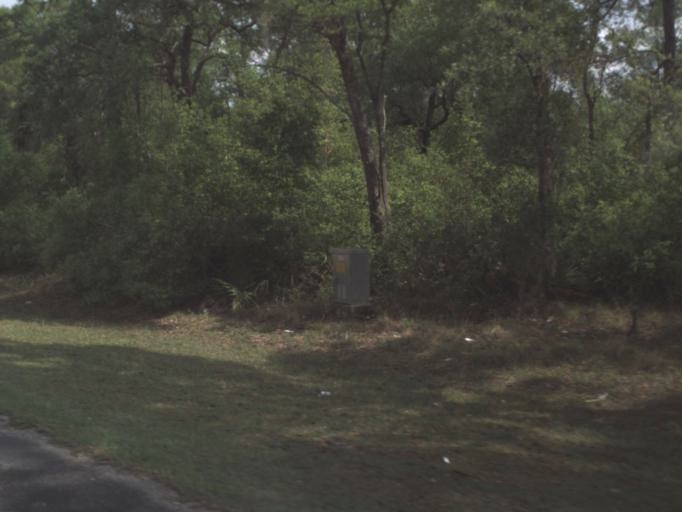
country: US
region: Florida
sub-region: Putnam County
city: Crescent City
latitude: 29.3611
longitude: -81.7353
